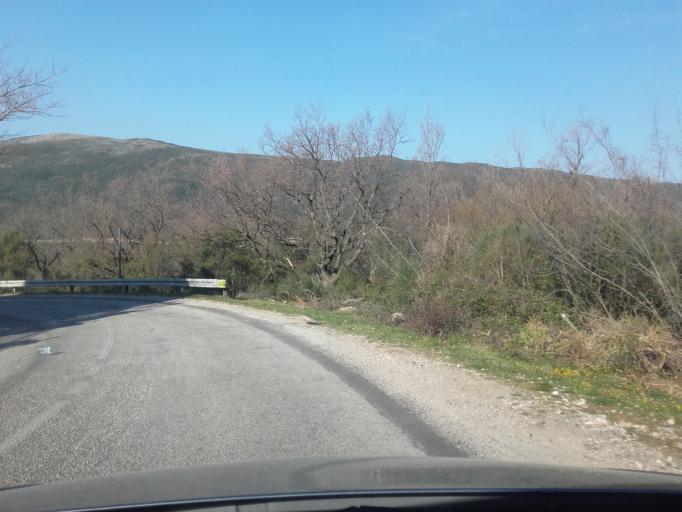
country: ME
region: Budva
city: Budva
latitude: 42.3055
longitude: 18.8093
